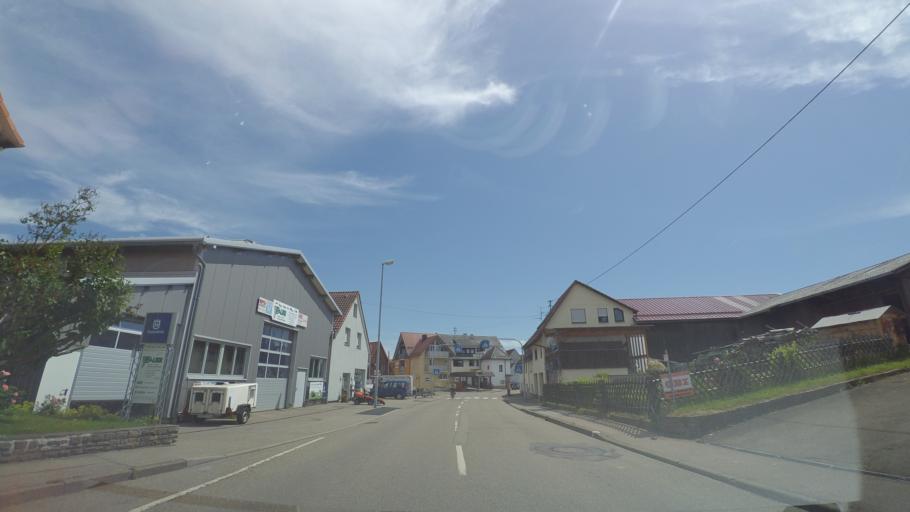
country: DE
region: Baden-Wuerttemberg
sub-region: Regierungsbezirk Stuttgart
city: Kaisersbach
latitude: 48.9307
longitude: 9.6389
